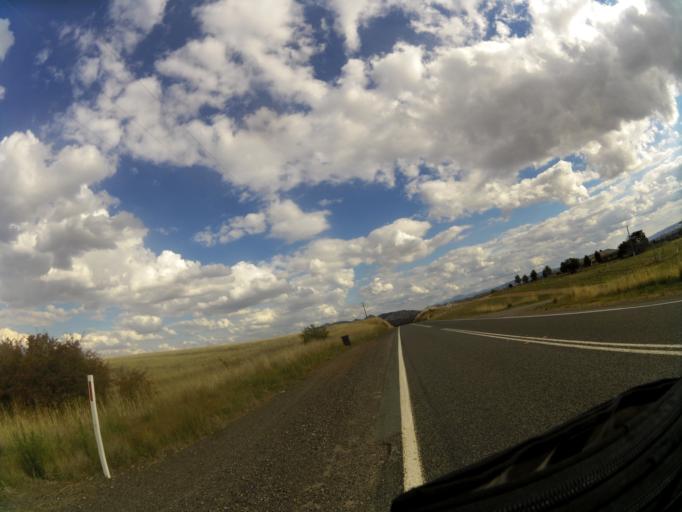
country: AU
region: Victoria
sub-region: Mansfield
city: Mansfield
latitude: -37.0238
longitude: 146.0940
